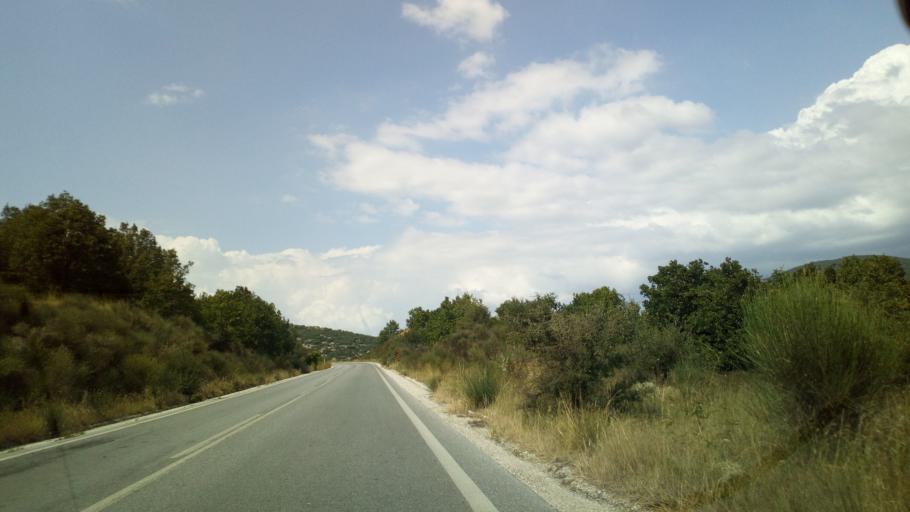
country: GR
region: Central Macedonia
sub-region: Nomos Chalkidikis
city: Polygyros
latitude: 40.4498
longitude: 23.4144
